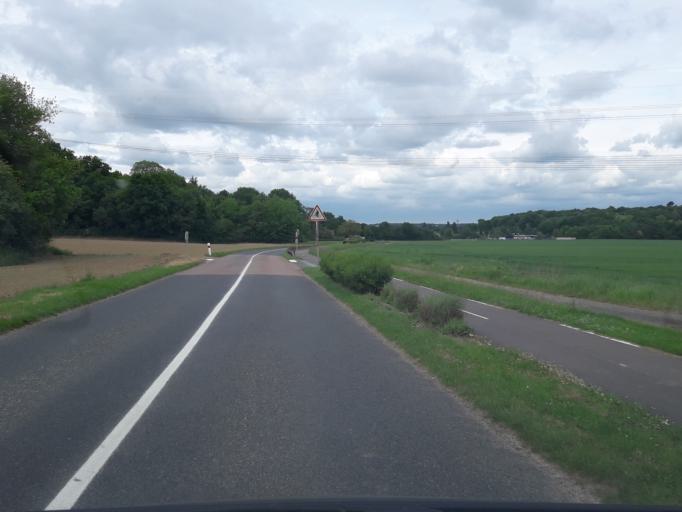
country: FR
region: Ile-de-France
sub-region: Departement de l'Essonne
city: Boissy-le-Cutte
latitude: 48.4495
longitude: 2.3066
